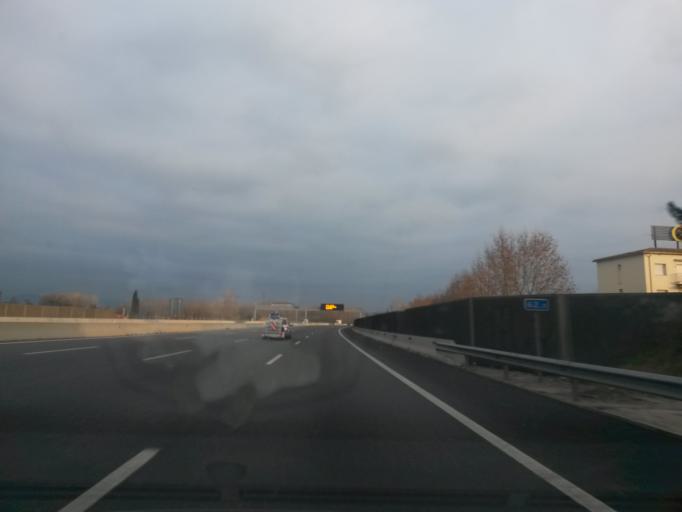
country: ES
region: Catalonia
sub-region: Provincia de Girona
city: Salt
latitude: 41.9738
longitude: 2.7785
